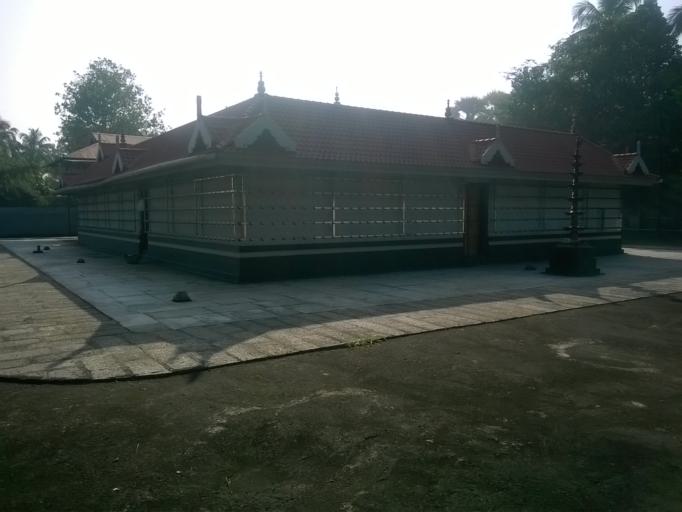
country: IN
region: Kerala
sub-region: Palakkad district
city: Shoranur
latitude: 10.7966
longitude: 76.2682
